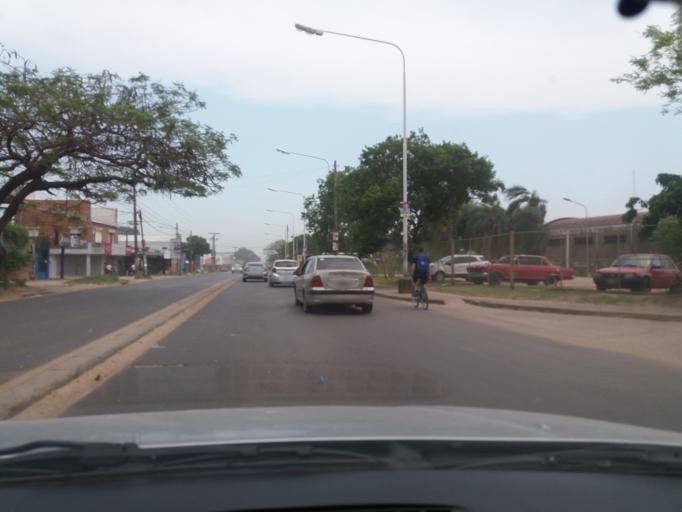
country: AR
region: Corrientes
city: Corrientes
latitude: -27.4976
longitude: -58.8156
